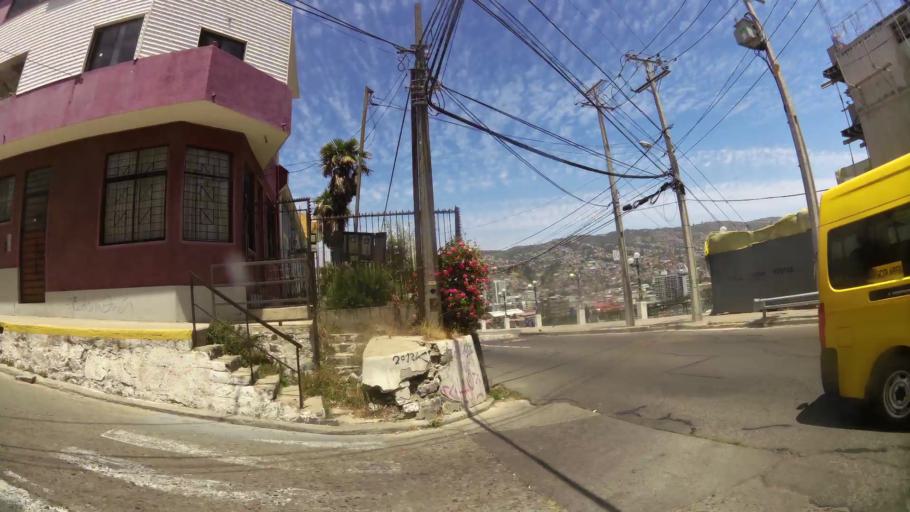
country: CL
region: Valparaiso
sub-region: Provincia de Valparaiso
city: Valparaiso
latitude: -33.0420
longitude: -71.6039
